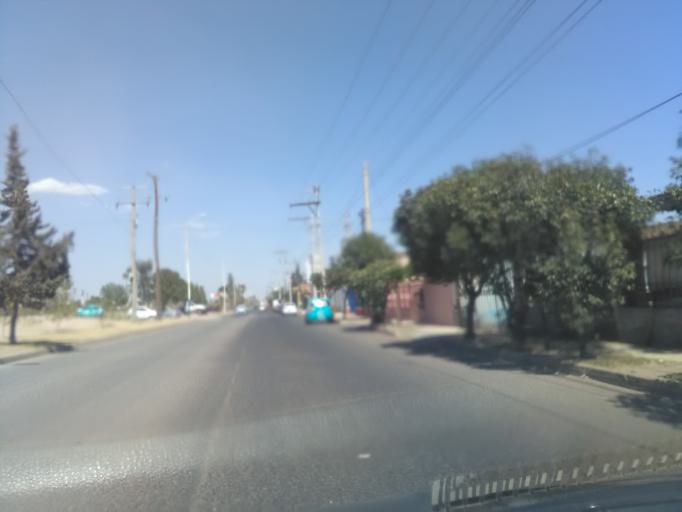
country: MX
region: Durango
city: Victoria de Durango
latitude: 24.0435
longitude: -104.6467
